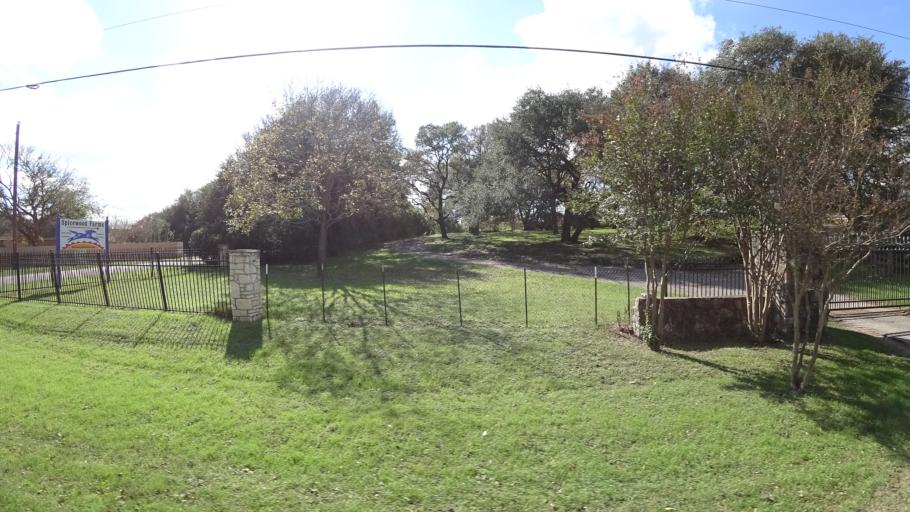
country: US
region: Texas
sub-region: Williamson County
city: Jollyville
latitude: 30.3966
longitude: -97.7779
